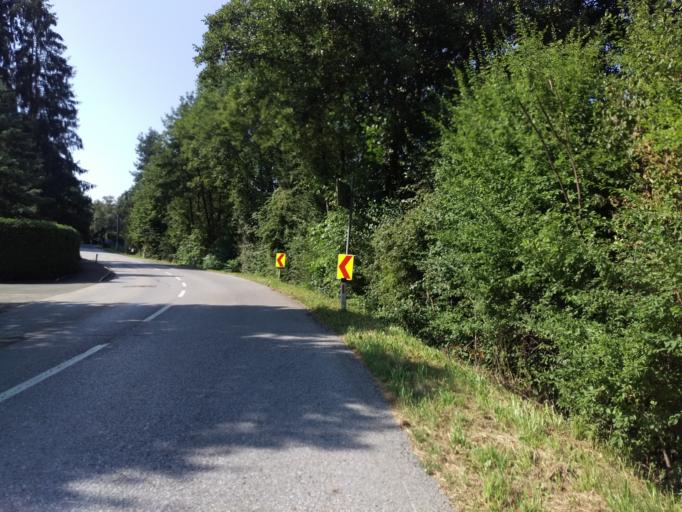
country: AT
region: Styria
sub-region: Politischer Bezirk Graz-Umgebung
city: Mellach
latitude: 46.9349
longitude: 15.5109
